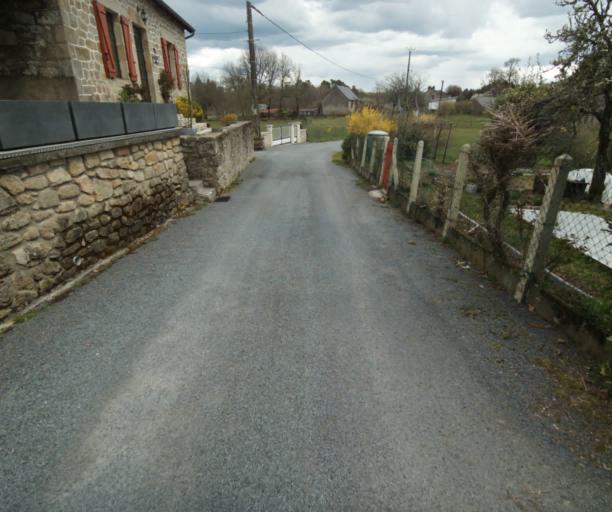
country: FR
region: Limousin
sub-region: Departement de la Correze
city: Correze
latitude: 45.2699
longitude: 1.9584
